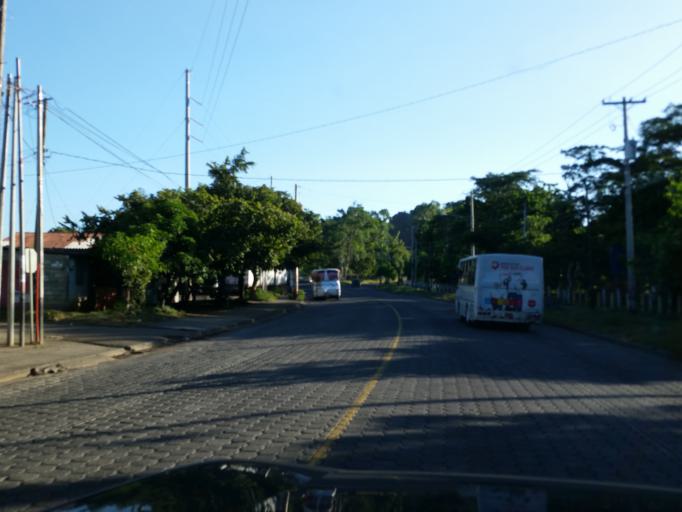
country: NI
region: Managua
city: Ciudad Sandino
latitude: 12.1396
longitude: -86.3077
